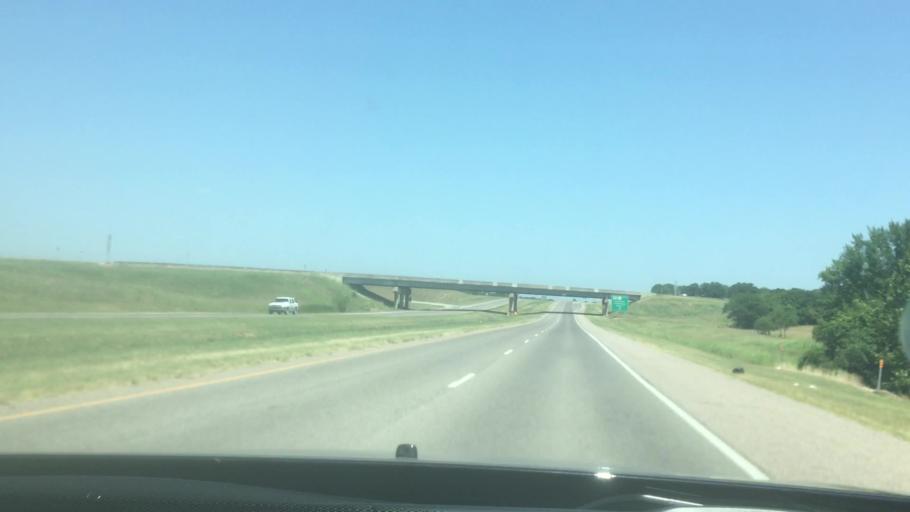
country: US
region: Oklahoma
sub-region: Pontotoc County
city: Ada
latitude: 34.7245
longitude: -96.6327
